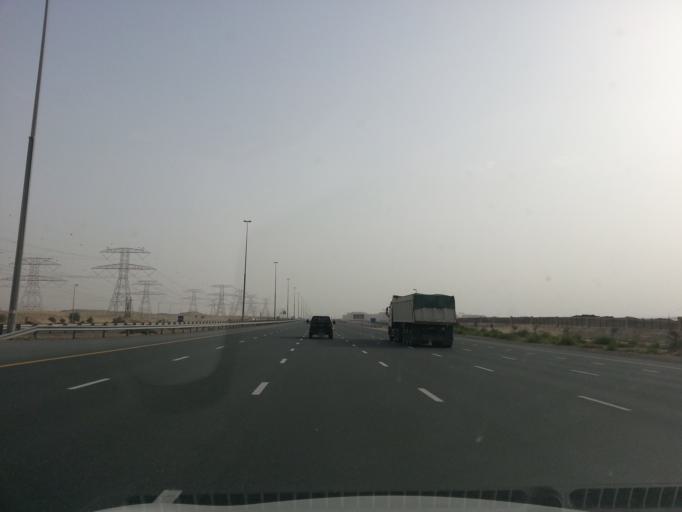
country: AE
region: Dubai
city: Dubai
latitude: 25.0130
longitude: 55.2711
